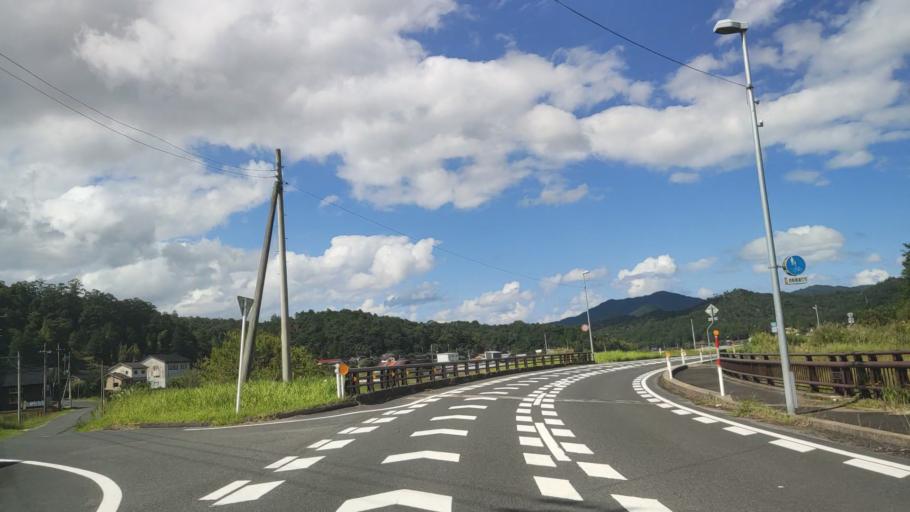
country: JP
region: Hyogo
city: Toyooka
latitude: 35.5661
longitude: 134.9737
